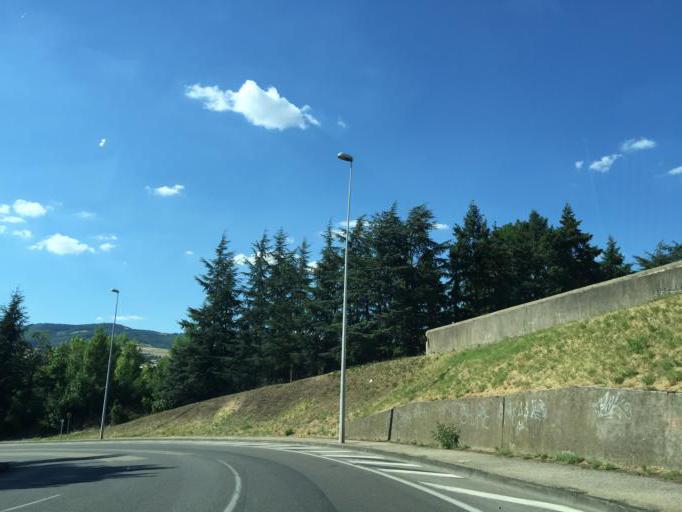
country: FR
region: Rhone-Alpes
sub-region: Departement de la Loire
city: Saint-Chamond
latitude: 45.4817
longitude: 4.5355
